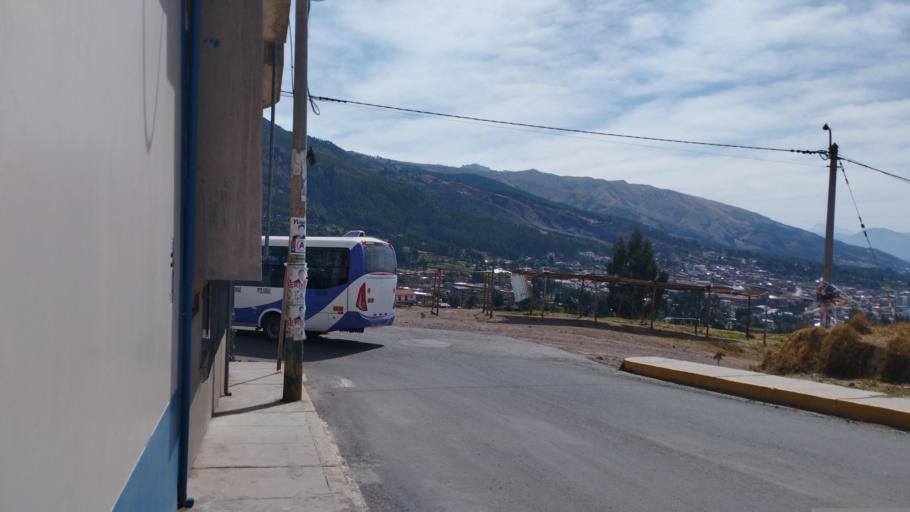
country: PE
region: Cusco
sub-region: Provincia de Cusco
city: Cusco
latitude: -13.5222
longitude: -71.9143
